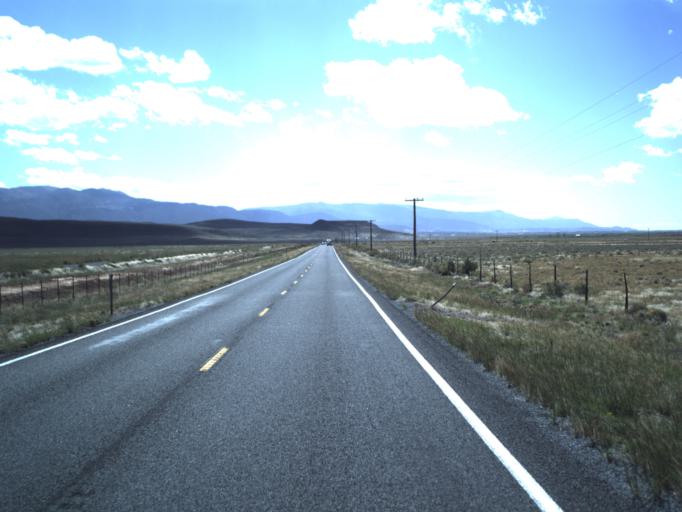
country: US
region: Utah
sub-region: Iron County
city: Enoch
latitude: 37.8850
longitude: -113.0316
